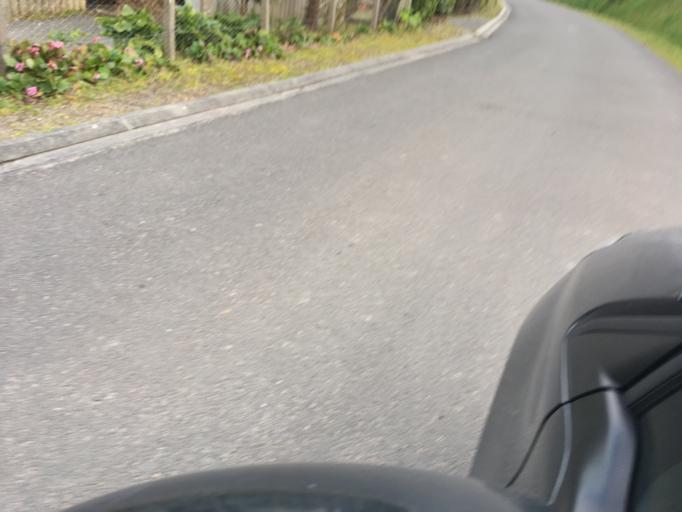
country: FR
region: Aquitaine
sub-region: Departement de la Gironde
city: Saint-Ciers-sur-Gironde
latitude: 45.3136
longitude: -0.6128
